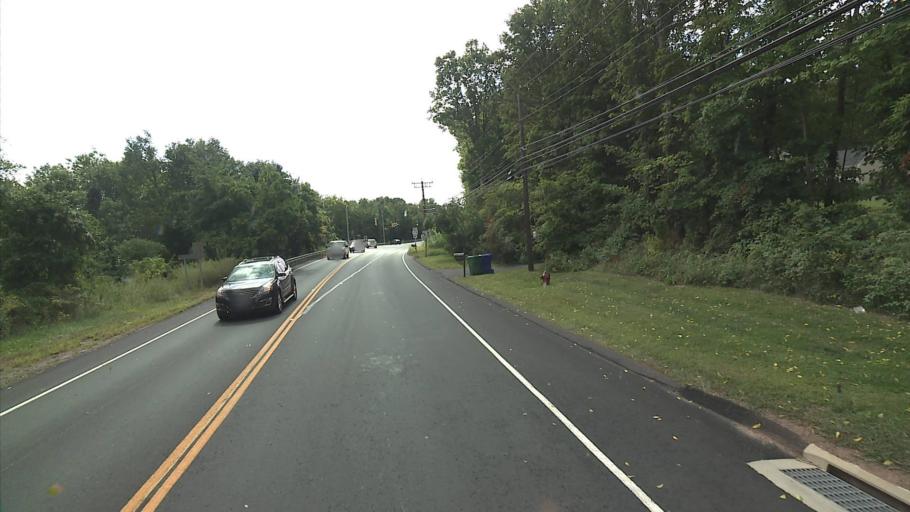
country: US
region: Connecticut
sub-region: Hartford County
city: Weatogue
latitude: 41.8290
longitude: -72.7706
